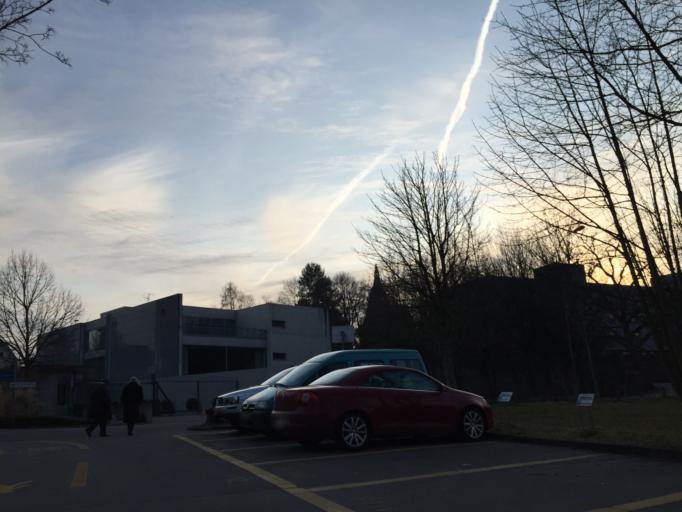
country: CH
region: Bern
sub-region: Bern-Mittelland District
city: Bern
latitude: 46.9614
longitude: 7.4393
